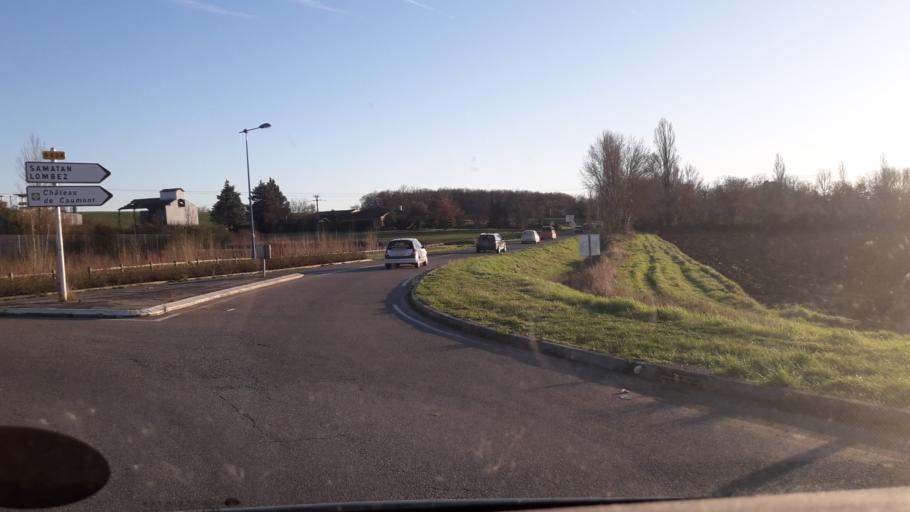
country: FR
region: Midi-Pyrenees
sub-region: Departement du Gers
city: Pujaudran
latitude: 43.6012
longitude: 1.0669
